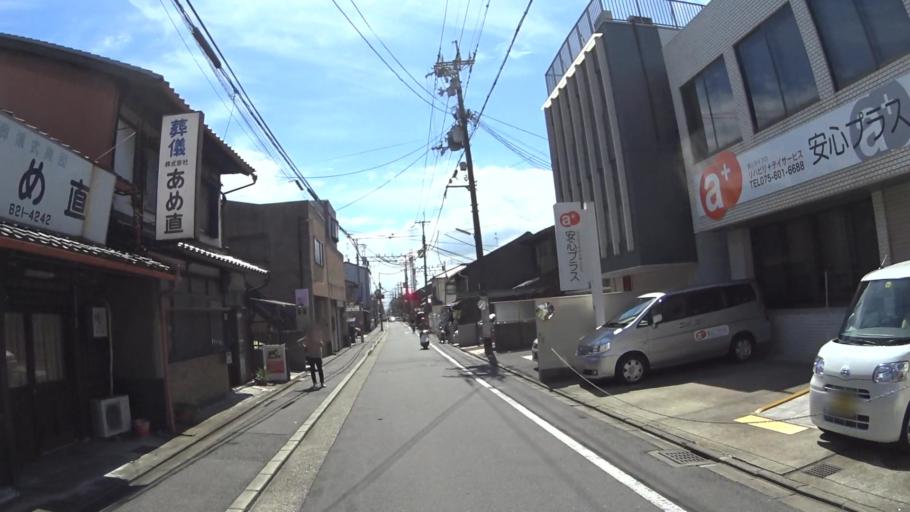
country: JP
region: Kyoto
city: Uji
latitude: 34.9371
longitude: 135.7649
